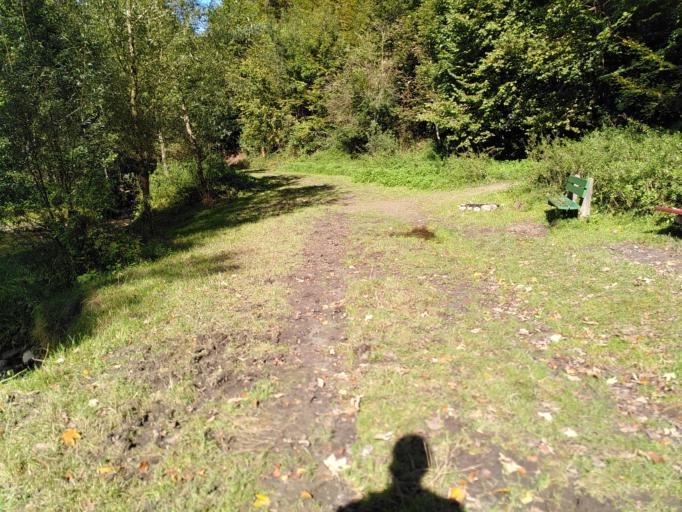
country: CH
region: Bern
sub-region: Oberaargau
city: Seeberg
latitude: 47.1308
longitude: 7.7052
